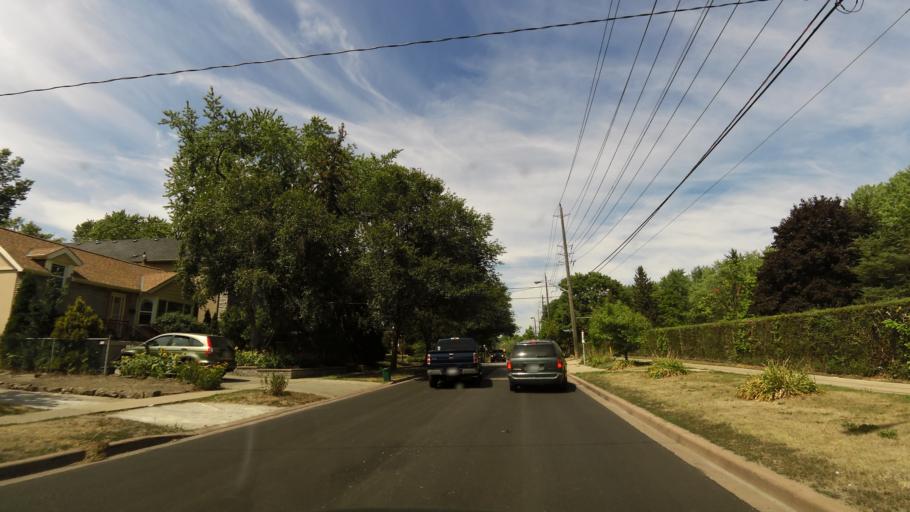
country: CA
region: Ontario
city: Etobicoke
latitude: 43.6466
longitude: -79.5046
